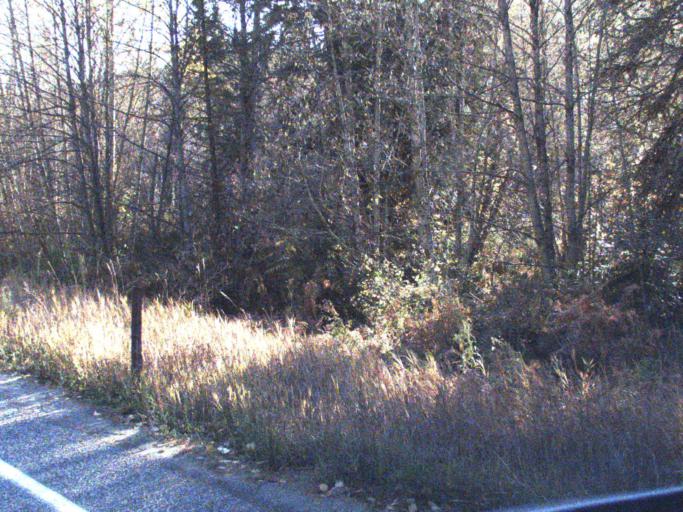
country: CA
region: British Columbia
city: Rossland
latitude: 48.9984
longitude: -117.8308
